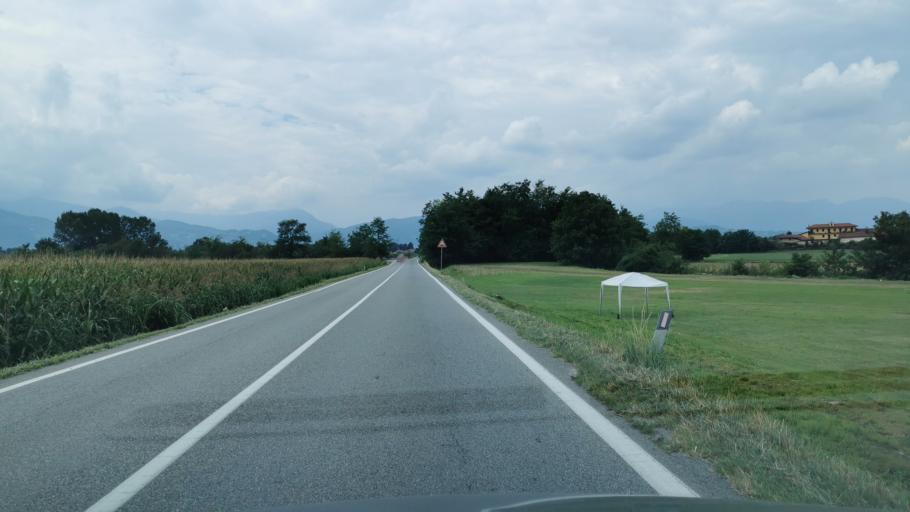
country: IT
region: Piedmont
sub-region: Provincia di Torino
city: Garzigliana
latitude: 44.8341
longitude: 7.3624
